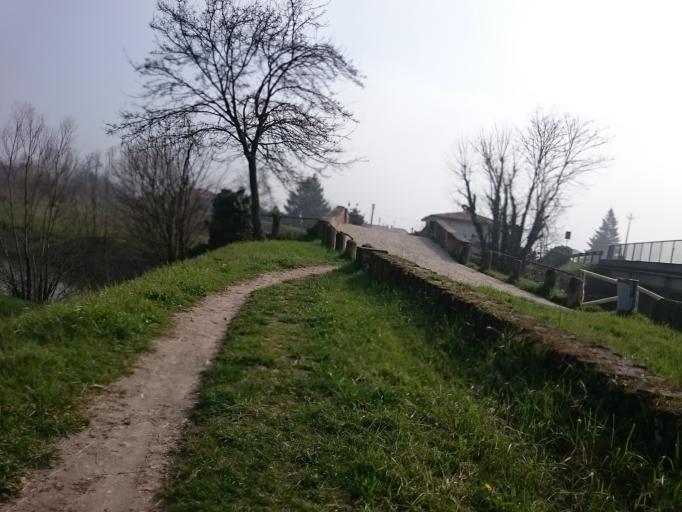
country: IT
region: Veneto
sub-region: Provincia di Padova
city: Due Carrare
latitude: 45.2836
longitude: 11.8320
